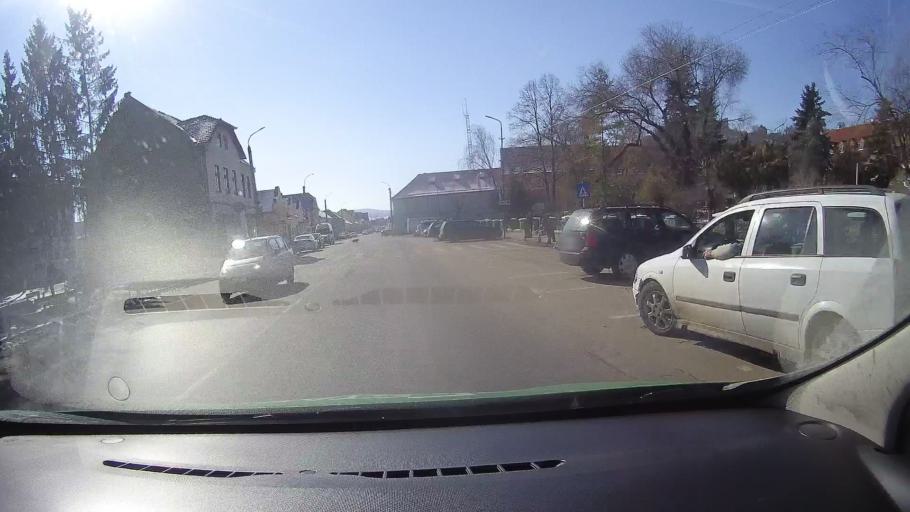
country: RO
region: Brasov
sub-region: Oras Rupea
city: Rupea
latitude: 46.0380
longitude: 25.2206
